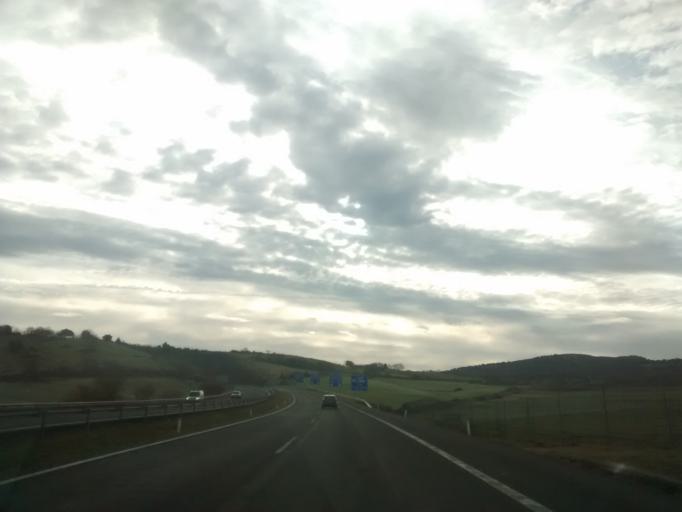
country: ES
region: Basque Country
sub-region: Provincia de Alava
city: Murguia
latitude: 42.9493
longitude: -2.7959
